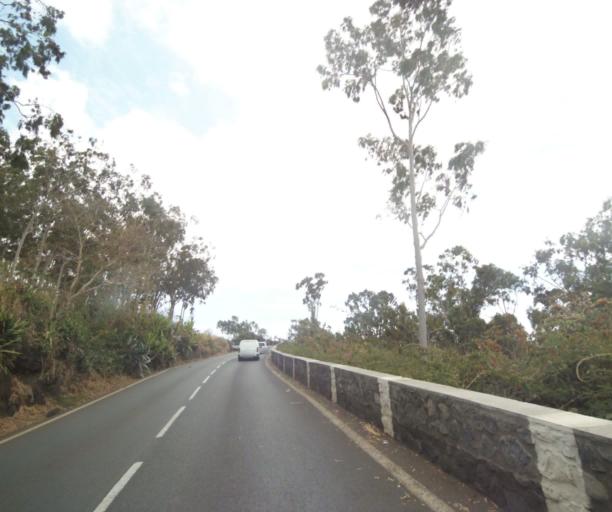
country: RE
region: Reunion
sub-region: Reunion
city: Saint-Paul
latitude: -21.0545
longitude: 55.2659
